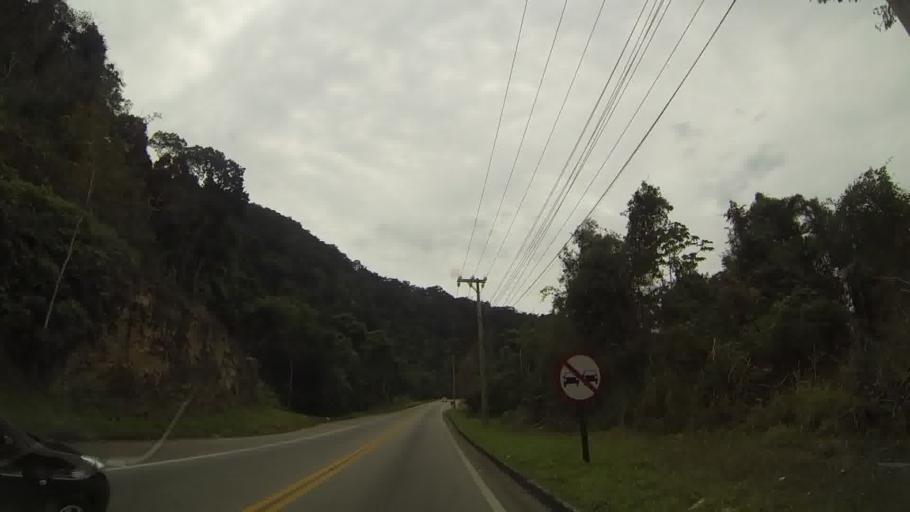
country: BR
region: Sao Paulo
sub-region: Sao Sebastiao
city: Sao Sebastiao
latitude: -23.8235
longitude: -45.4459
